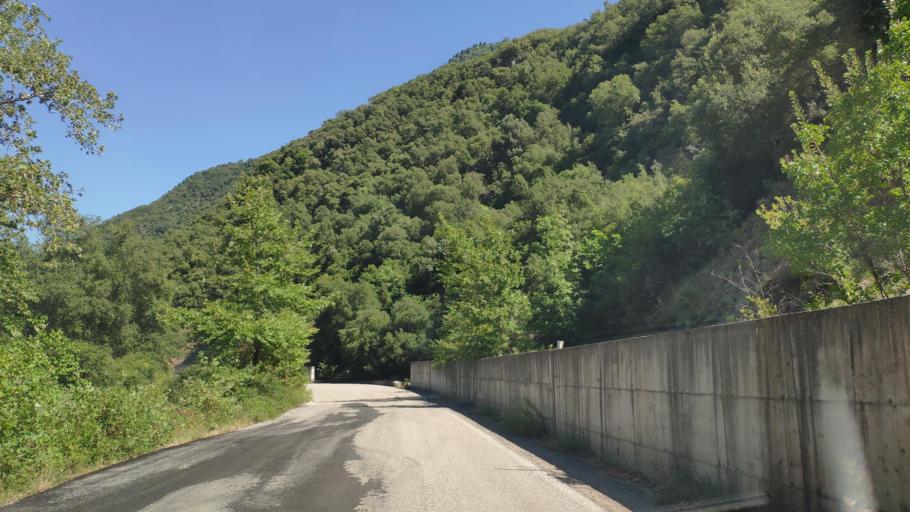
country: GR
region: Central Greece
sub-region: Nomos Evrytanias
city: Kerasochori
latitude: 39.0232
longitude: 21.6017
